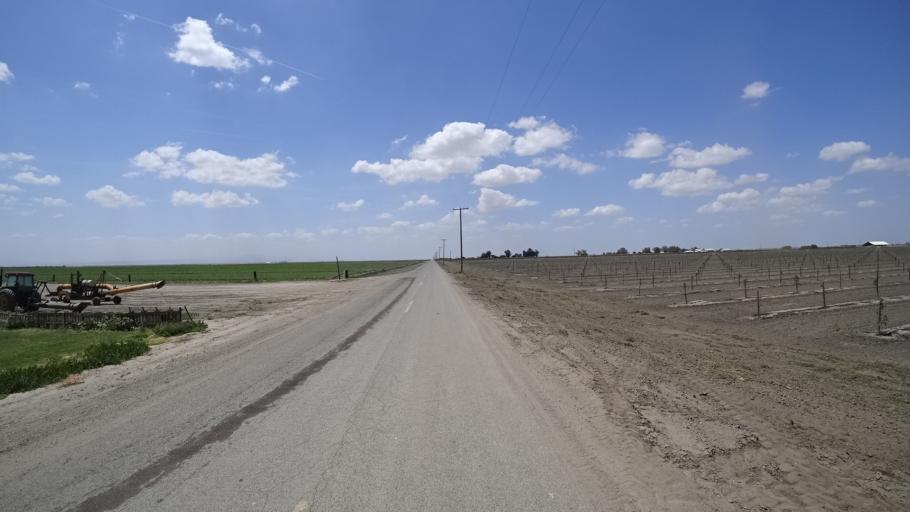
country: US
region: California
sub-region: Kings County
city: Stratford
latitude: 36.1526
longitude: -119.8018
